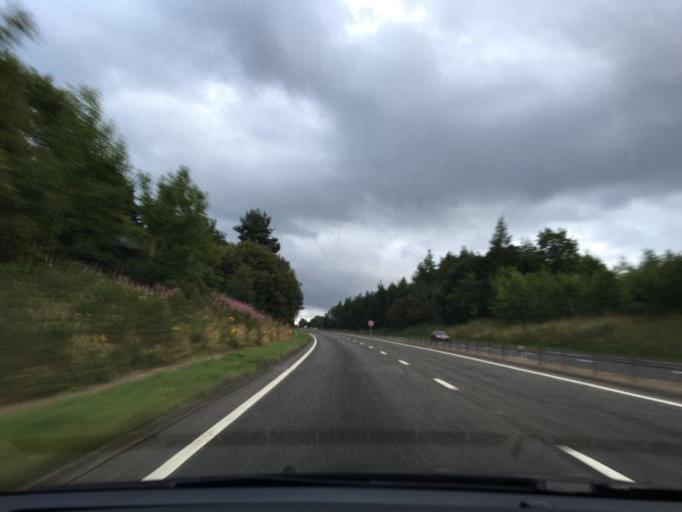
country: GB
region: Scotland
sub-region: Highland
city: Inverness
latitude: 57.4569
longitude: -4.1652
